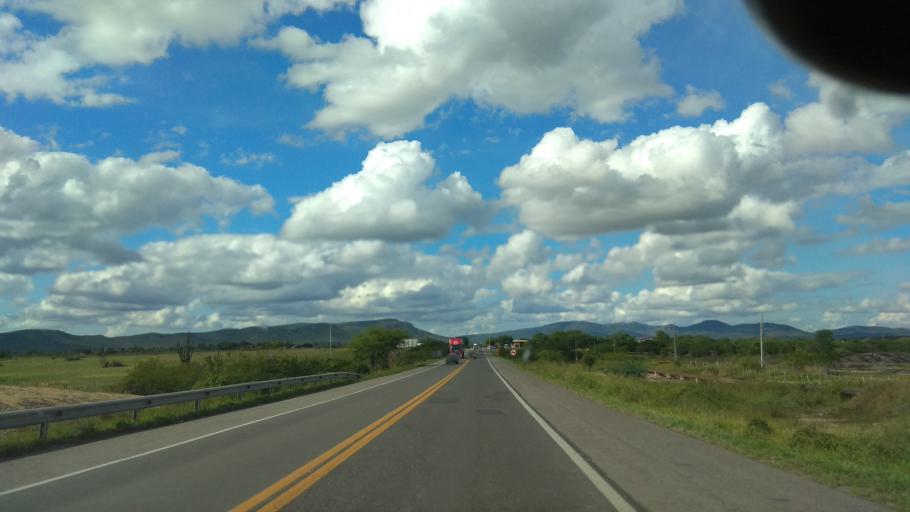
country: BR
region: Bahia
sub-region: Castro Alves
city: Castro Alves
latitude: -12.6867
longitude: -39.6839
